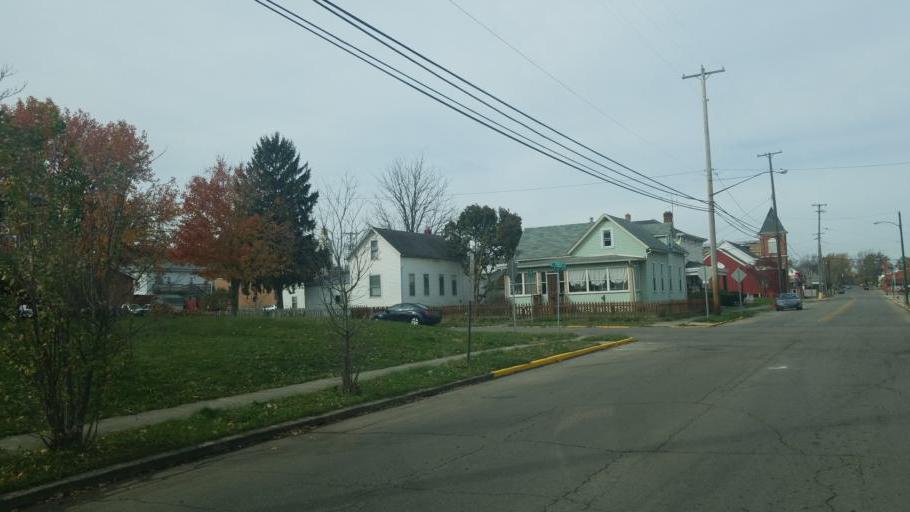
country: US
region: Ohio
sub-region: Madison County
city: London
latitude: 39.8860
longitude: -83.4446
